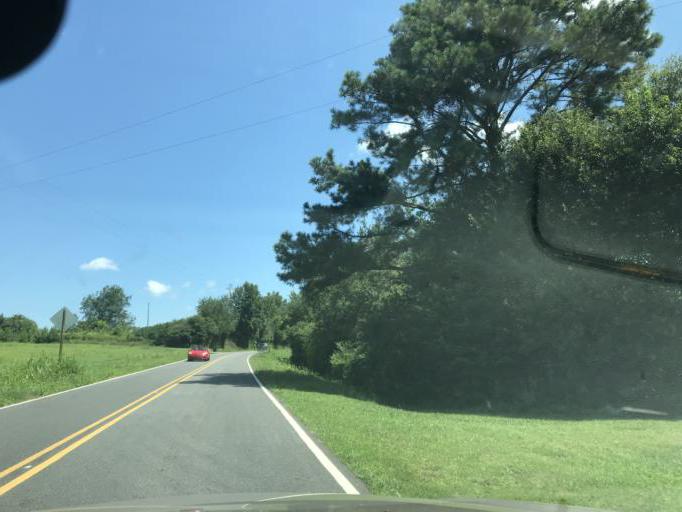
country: US
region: Georgia
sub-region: Dawson County
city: Dawsonville
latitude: 34.3300
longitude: -84.0488
